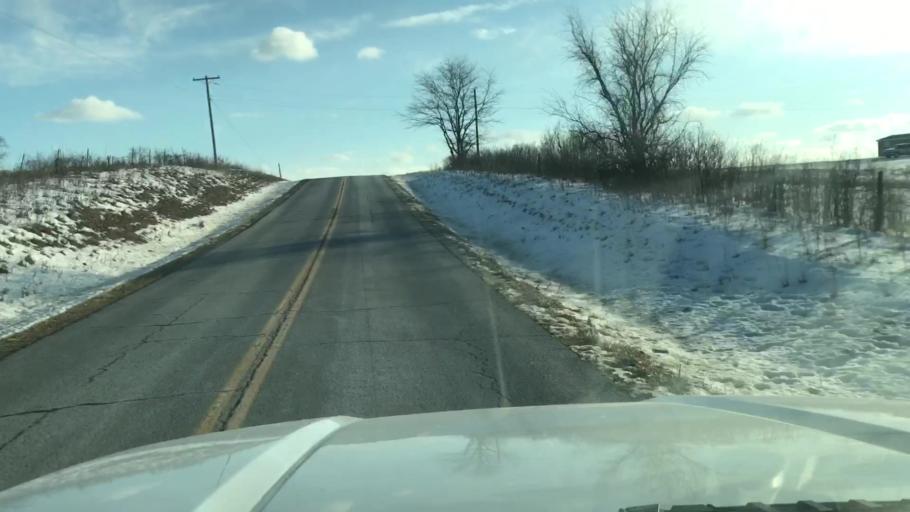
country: US
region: Missouri
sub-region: Holt County
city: Oregon
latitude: 40.0627
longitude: -94.9749
